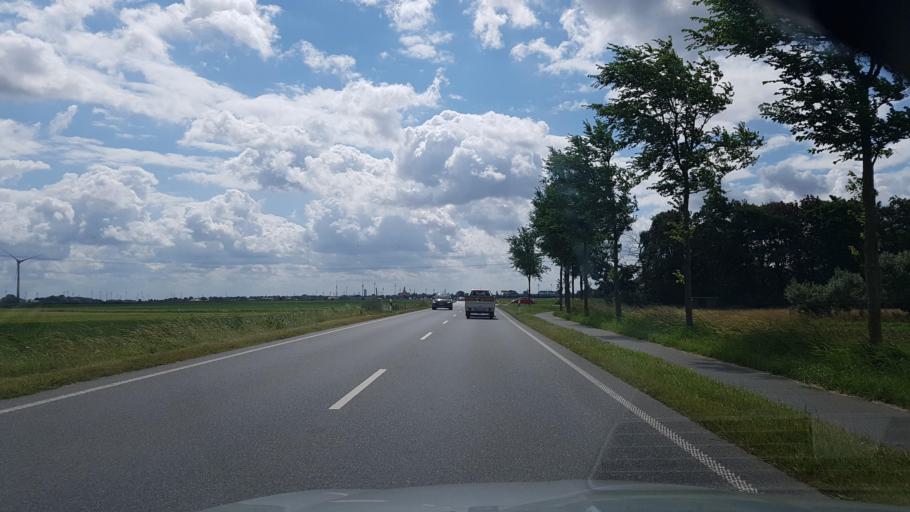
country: DE
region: Schleswig-Holstein
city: Norddeich
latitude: 54.2299
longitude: 8.8962
